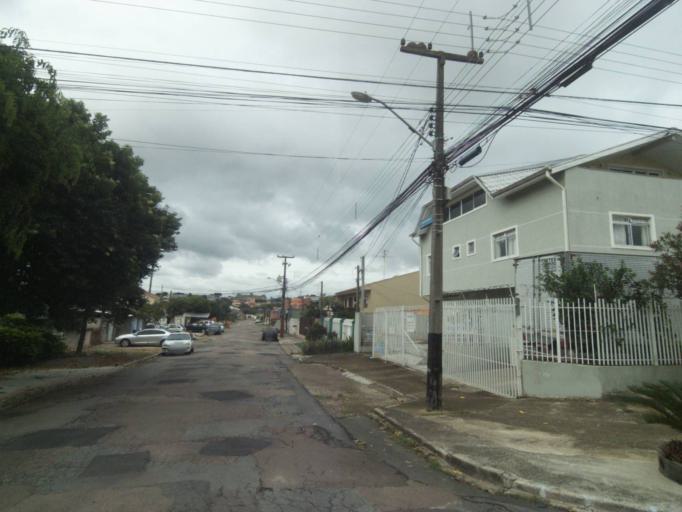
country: BR
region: Parana
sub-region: Curitiba
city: Curitiba
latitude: -25.4883
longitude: -49.3084
